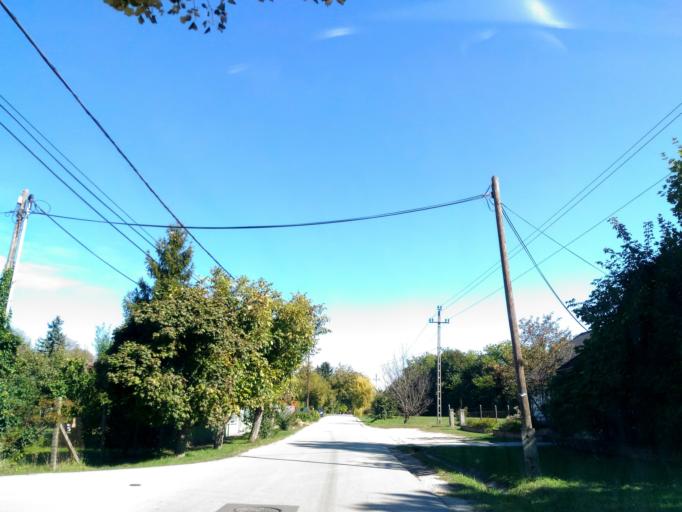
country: HU
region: Fejer
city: Gardony
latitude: 47.1930
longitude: 18.6096
